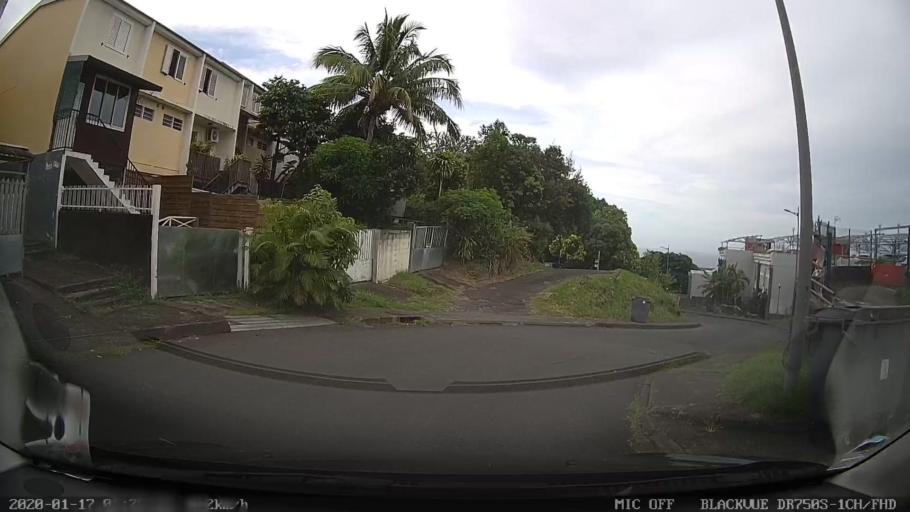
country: RE
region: Reunion
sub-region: Reunion
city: Saint-Denis
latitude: -20.9141
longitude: 55.4869
